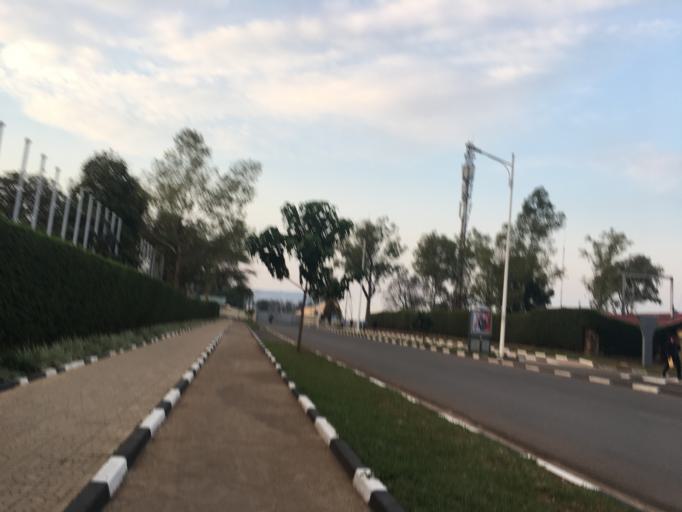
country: RW
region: Kigali
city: Kigali
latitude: -1.9565
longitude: 30.0622
